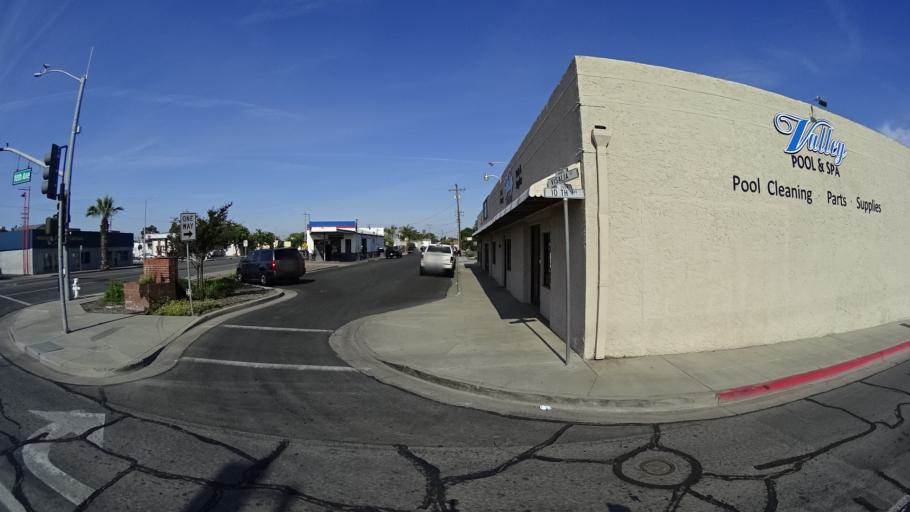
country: US
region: California
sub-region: Kings County
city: Hanford
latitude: 36.3282
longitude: -119.6370
